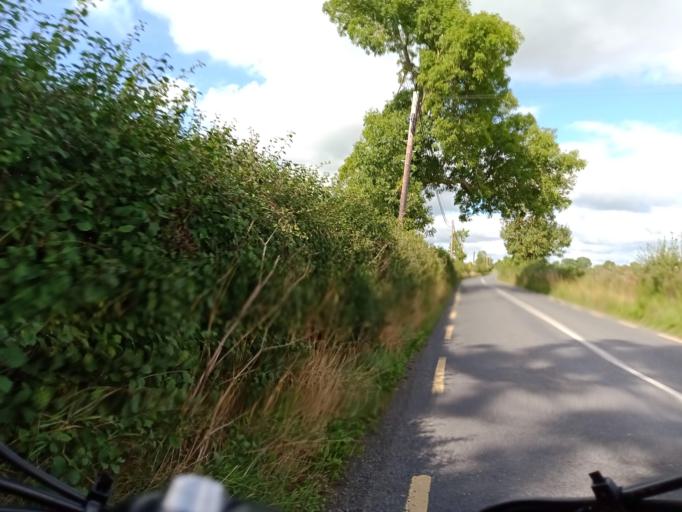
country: IE
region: Leinster
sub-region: Kilkenny
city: Kilkenny
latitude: 52.5717
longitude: -7.2791
